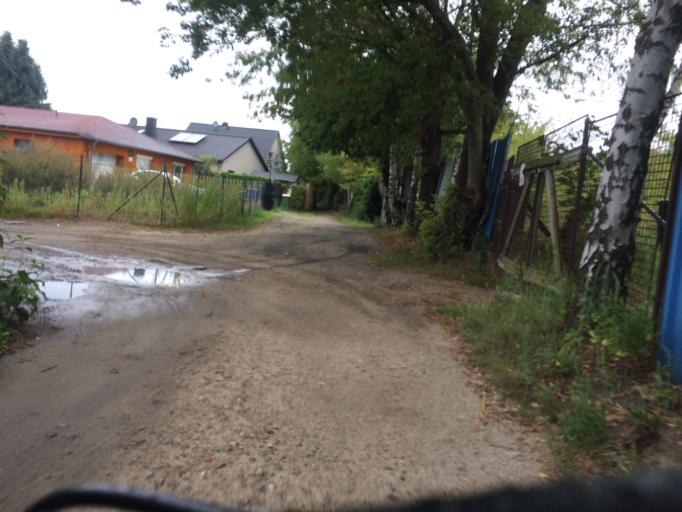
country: DE
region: Berlin
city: Buchholz
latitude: 52.5959
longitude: 13.4209
